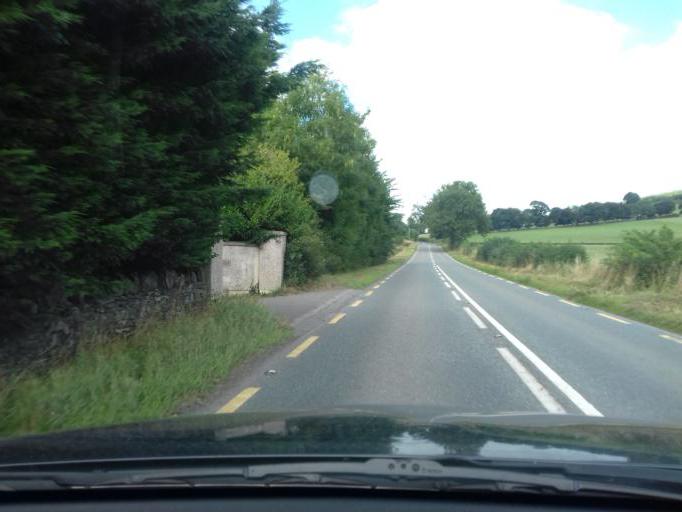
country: IE
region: Leinster
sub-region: Wicklow
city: Baltinglass
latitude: 52.9691
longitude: -6.6915
